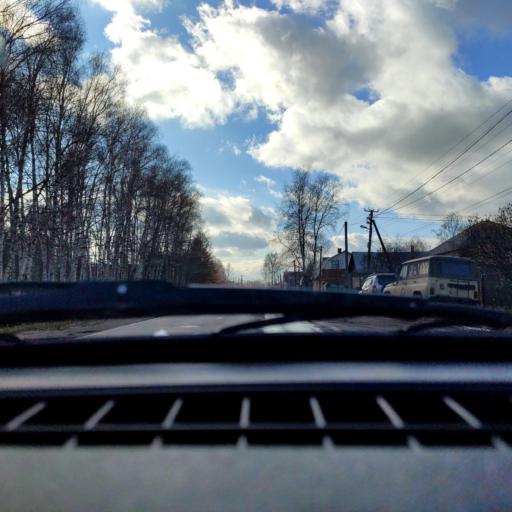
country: RU
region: Bashkortostan
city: Ufa
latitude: 54.8156
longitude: 56.1658
